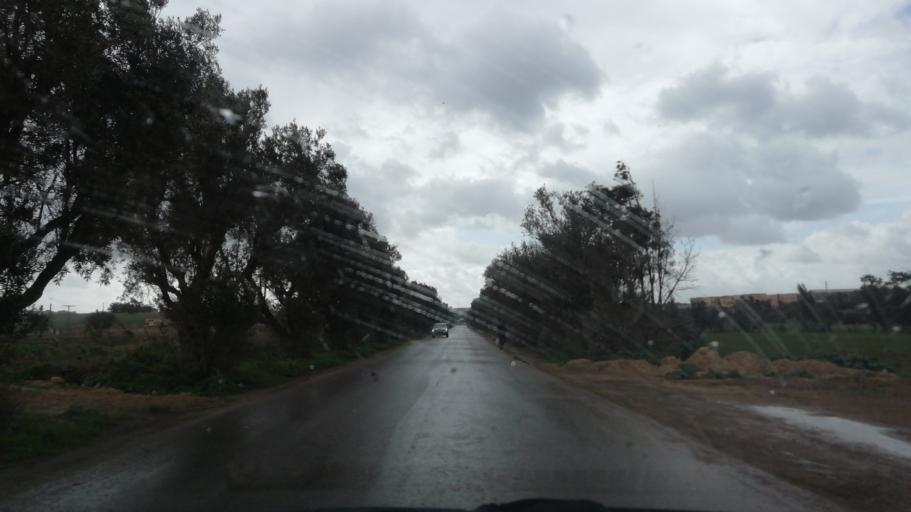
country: DZ
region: Oran
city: Sidi ech Chahmi
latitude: 35.6390
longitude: -0.5257
